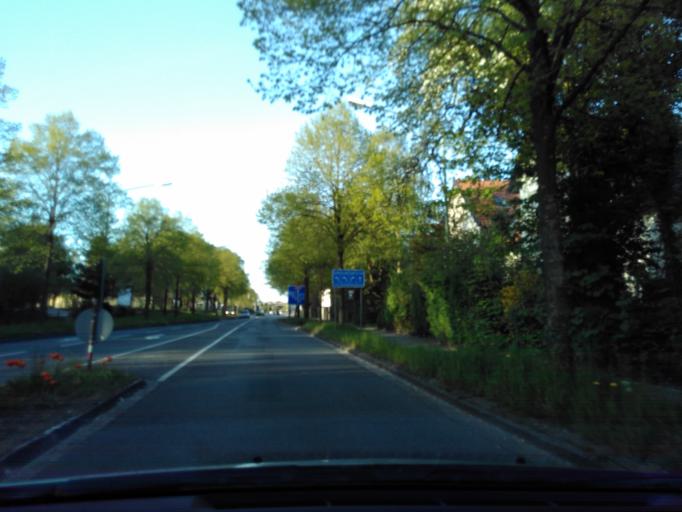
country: DE
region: Lower Saxony
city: Osnabrueck
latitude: 52.2604
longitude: 7.9996
